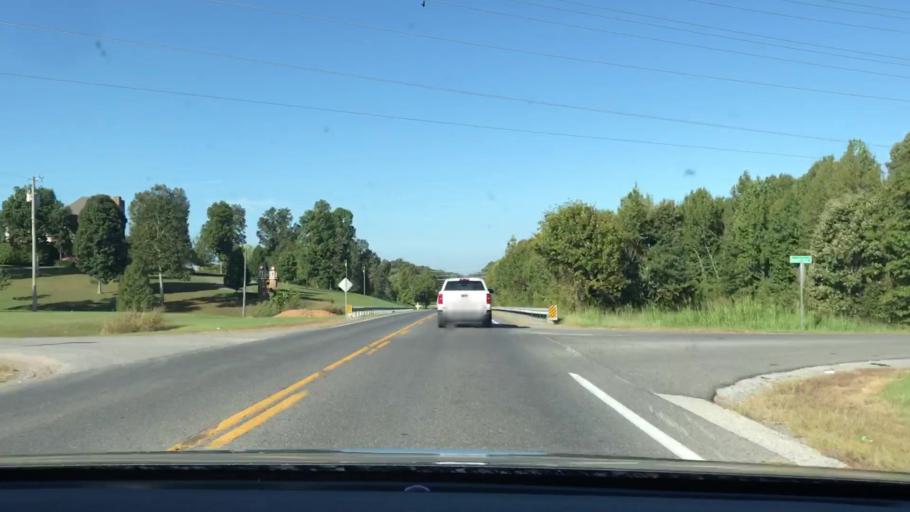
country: US
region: Kentucky
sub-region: Marshall County
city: Calvert City
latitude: 37.0049
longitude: -88.3851
